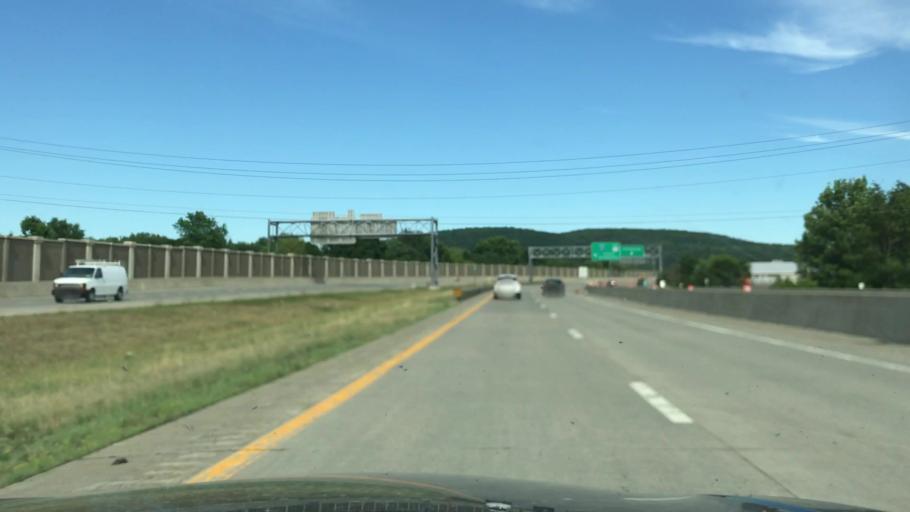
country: US
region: New York
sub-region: Chemung County
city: Horseheads
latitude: 42.1598
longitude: -76.8333
